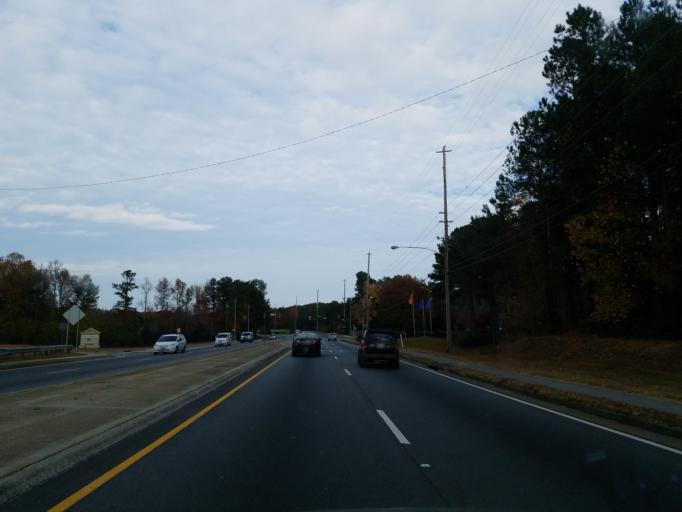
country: US
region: Georgia
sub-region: Cobb County
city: Mableton
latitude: 33.8678
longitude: -84.5925
